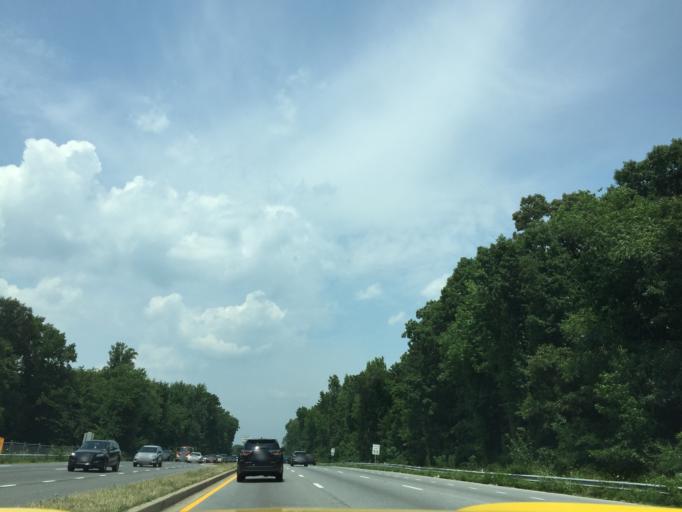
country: US
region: Maryland
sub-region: Prince George's County
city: Fort Washington
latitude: 38.7135
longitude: -76.9899
